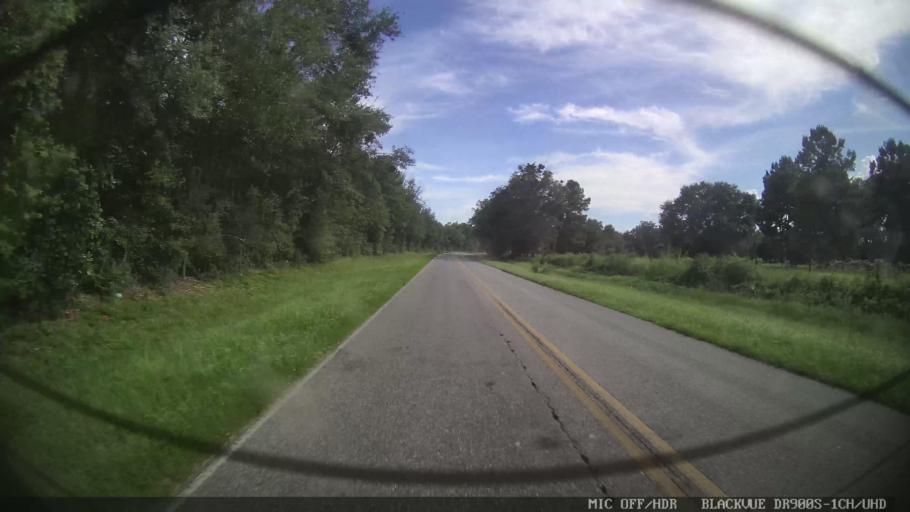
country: US
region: Georgia
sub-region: Echols County
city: Statenville
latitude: 30.6125
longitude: -83.2179
